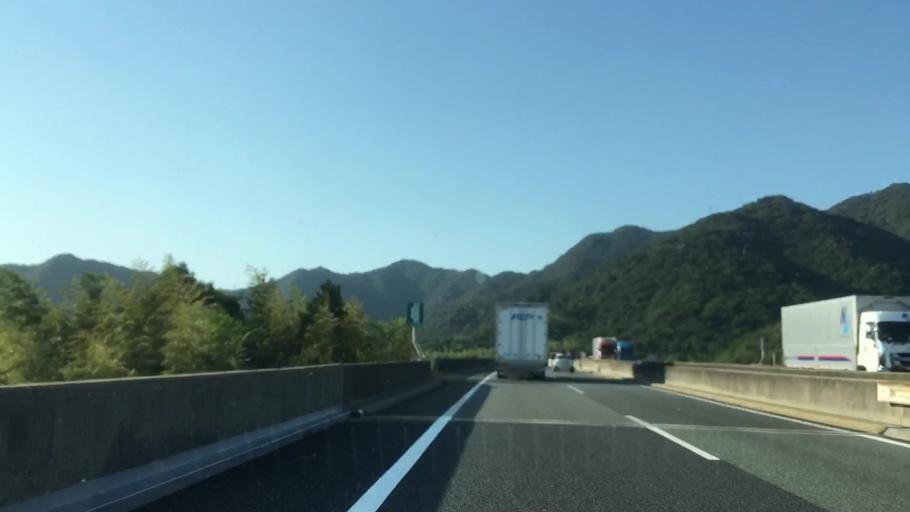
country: JP
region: Yamaguchi
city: Ogori-shimogo
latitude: 34.0953
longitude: 131.4540
